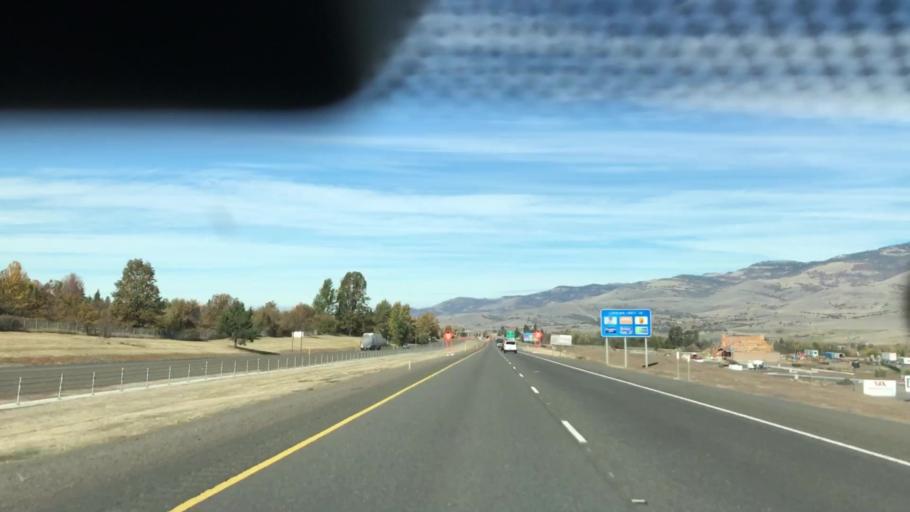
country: US
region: Oregon
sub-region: Jackson County
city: Ashland
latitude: 42.1641
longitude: -122.6517
